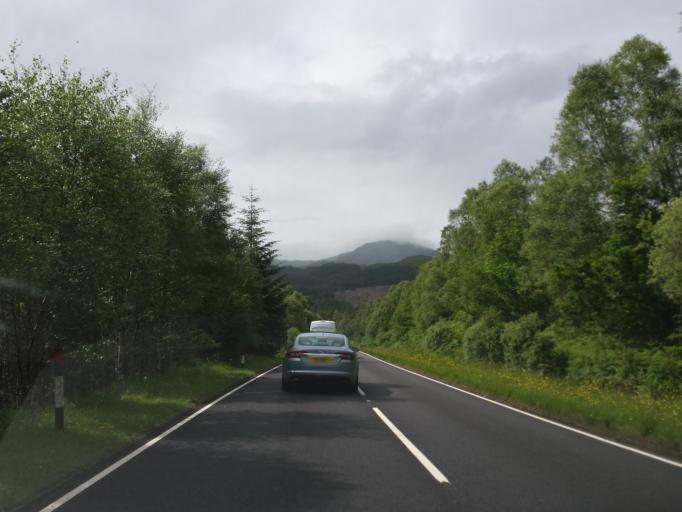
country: GB
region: Scotland
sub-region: Highland
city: Fort William
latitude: 56.8628
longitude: -5.3817
